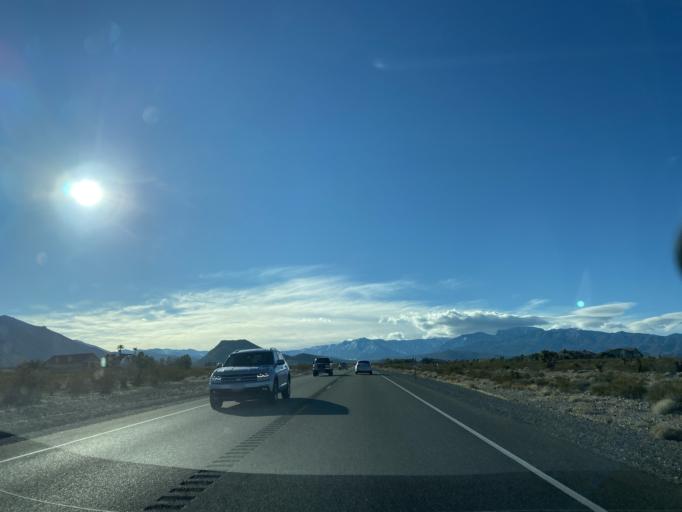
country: US
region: Nevada
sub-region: Clark County
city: Summerlin South
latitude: 36.3171
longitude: -115.3683
